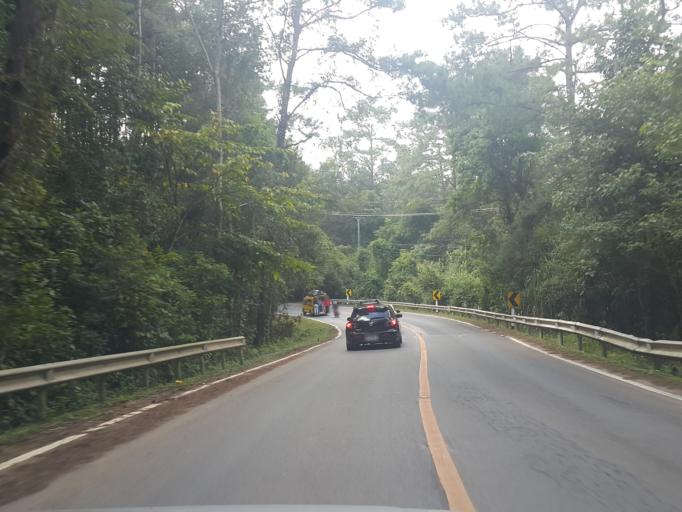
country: TH
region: Chiang Mai
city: Chom Thong
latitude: 18.5436
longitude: 98.5634
